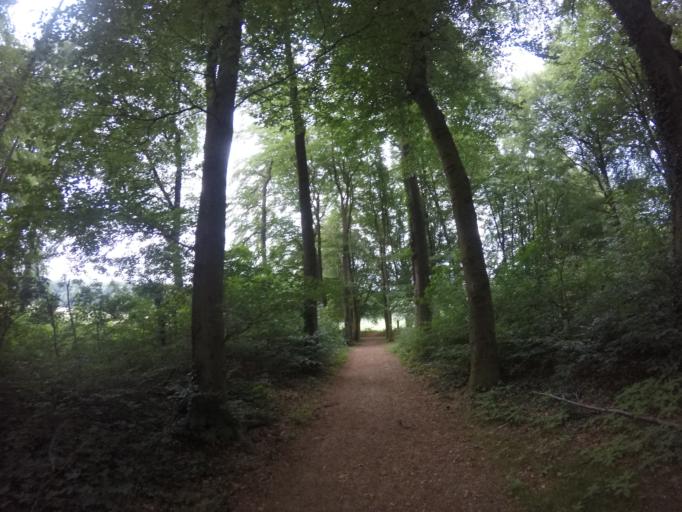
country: NL
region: Gelderland
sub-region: Gemeente Renkum
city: Oosterbeek
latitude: 51.9909
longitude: 5.8623
